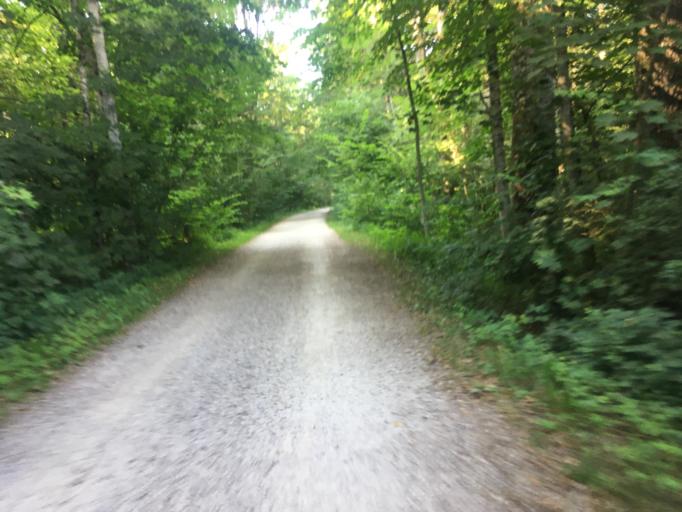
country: CH
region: Bern
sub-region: Emmental District
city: Oberburg
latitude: 47.0457
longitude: 7.6324
